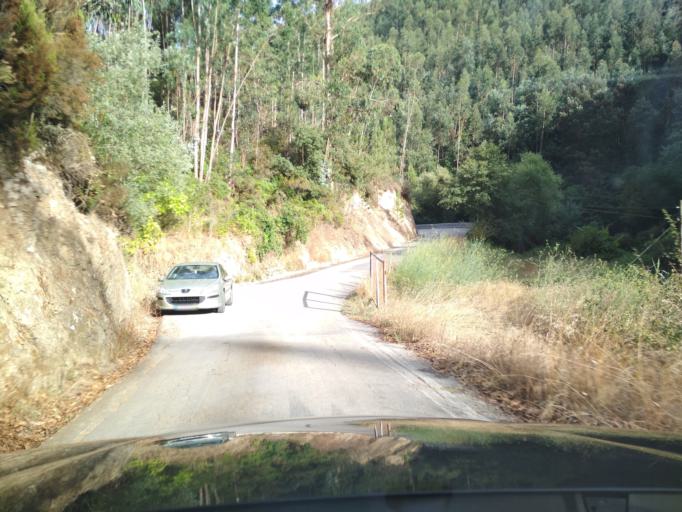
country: PT
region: Coimbra
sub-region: Coimbra
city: Coimbra
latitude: 40.2505
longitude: -8.3864
